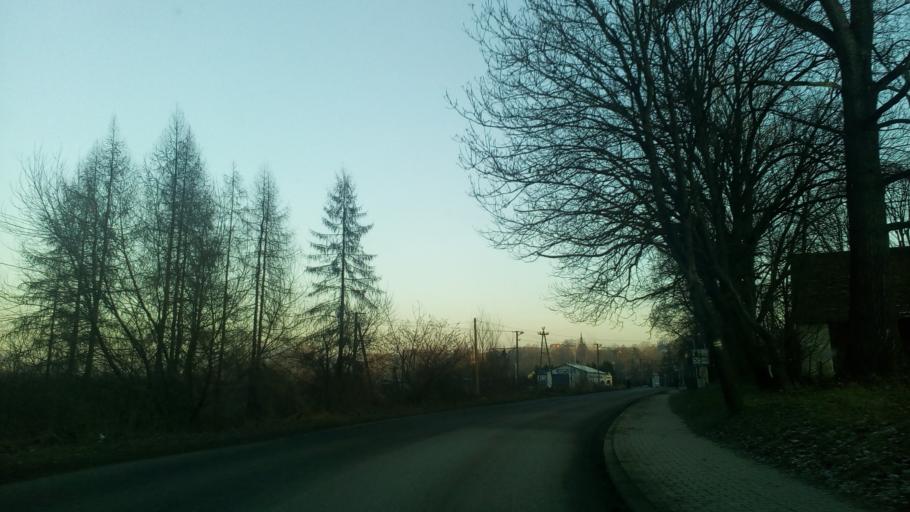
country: PL
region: Lesser Poland Voivodeship
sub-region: Powiat nowosadecki
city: Chelmiec
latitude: 49.6699
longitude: 20.6481
